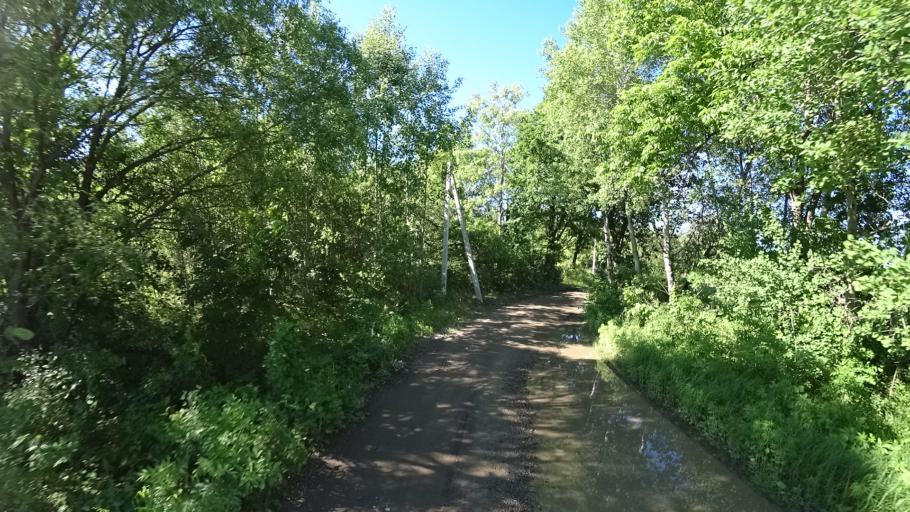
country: RU
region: Khabarovsk Krai
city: Khor
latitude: 47.8870
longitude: 135.0194
